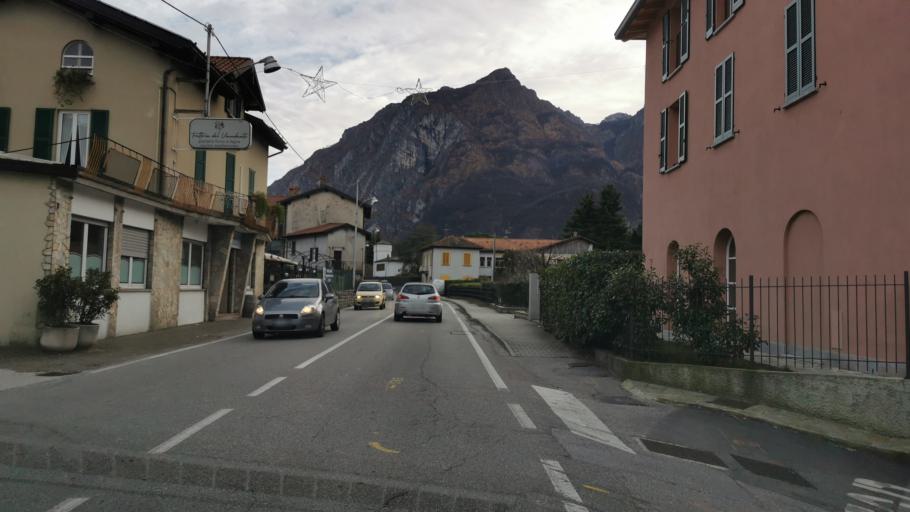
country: IT
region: Lombardy
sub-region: Provincia di Lecco
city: Abbadia Lariana
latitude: 45.8978
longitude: 9.3327
